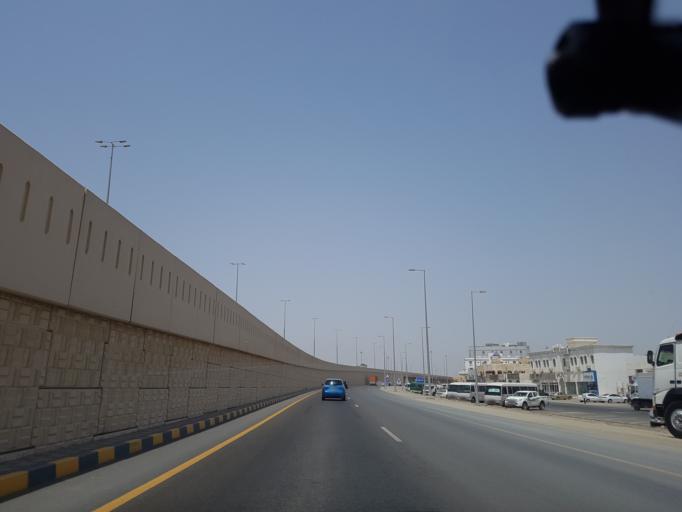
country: OM
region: Al Batinah
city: Al Liwa'
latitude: 24.4222
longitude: 56.6158
